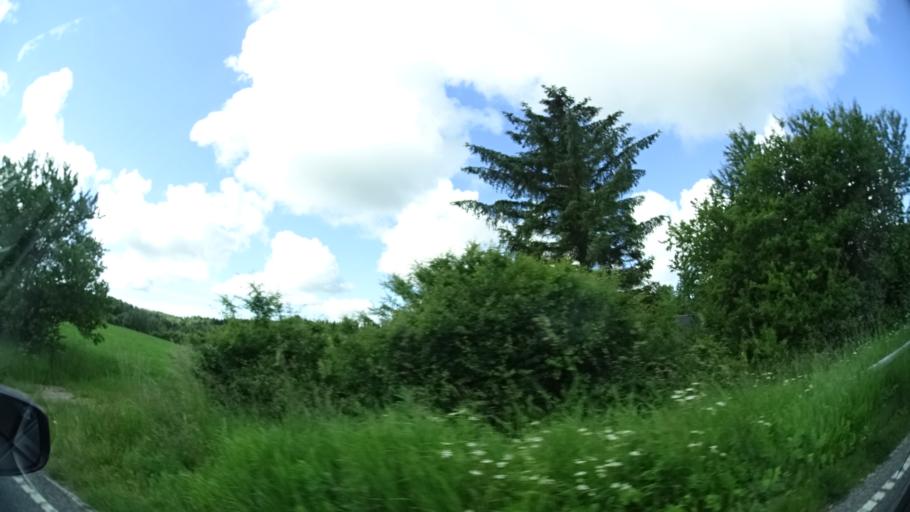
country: DK
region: Central Jutland
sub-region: Syddjurs Kommune
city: Ebeltoft
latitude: 56.2754
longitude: 10.5990
